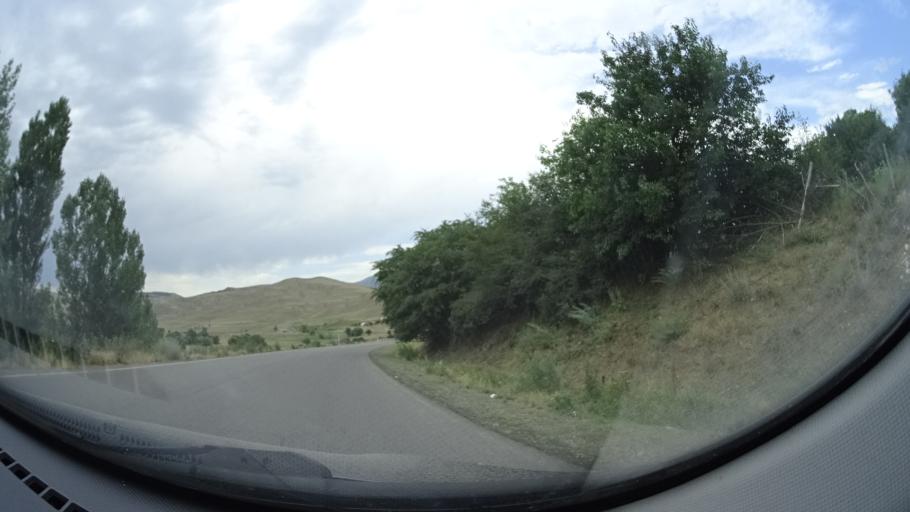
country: GE
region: Samtskhe-Javakheti
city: Aspindza
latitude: 41.5897
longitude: 43.2274
